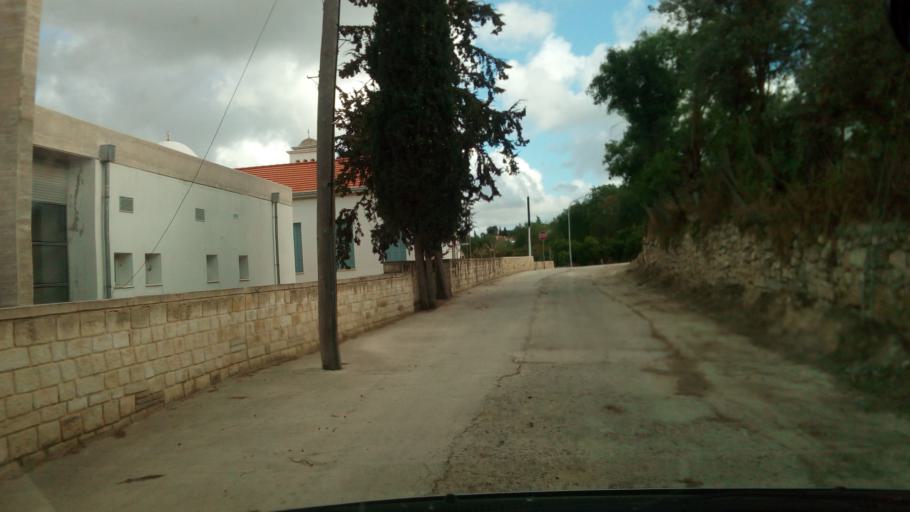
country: CY
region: Pafos
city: Mesogi
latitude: 34.8582
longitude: 32.5120
